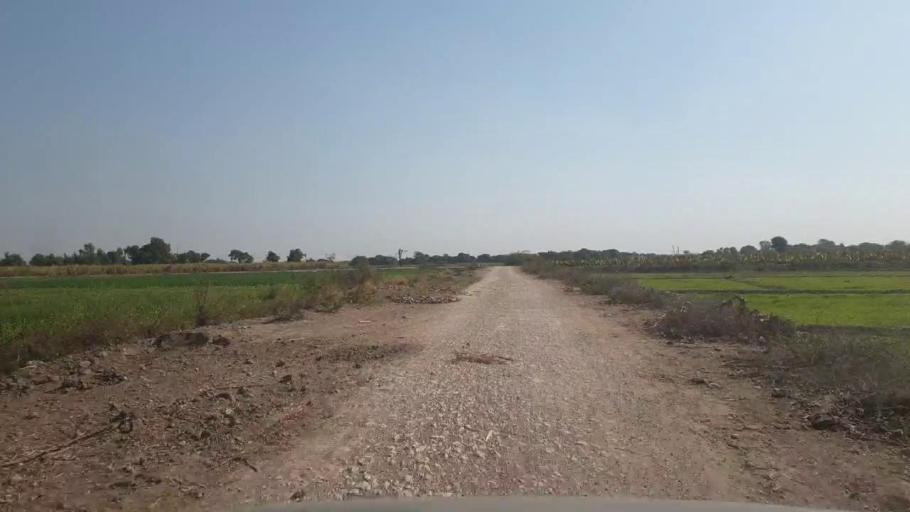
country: PK
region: Sindh
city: Chambar
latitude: 25.3139
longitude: 68.8734
